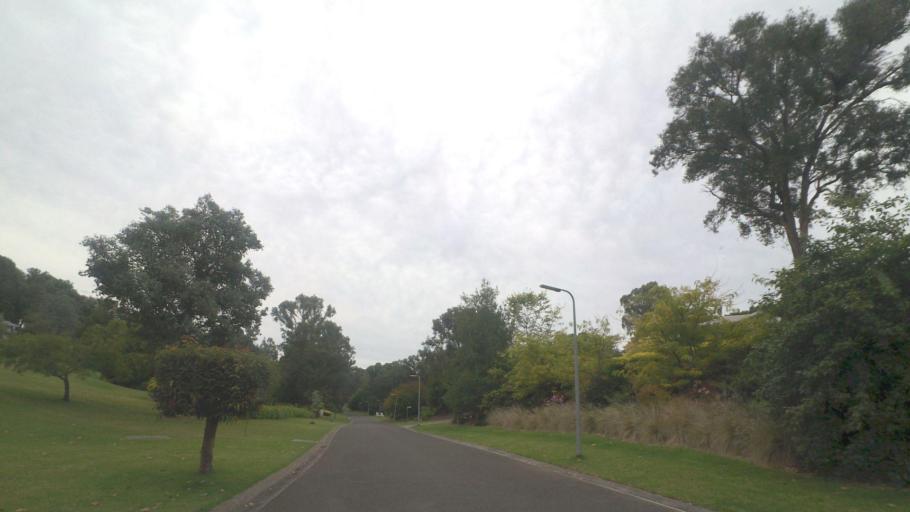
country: AU
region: Victoria
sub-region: Nillumbik
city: North Warrandyte
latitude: -37.7448
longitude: 145.1914
